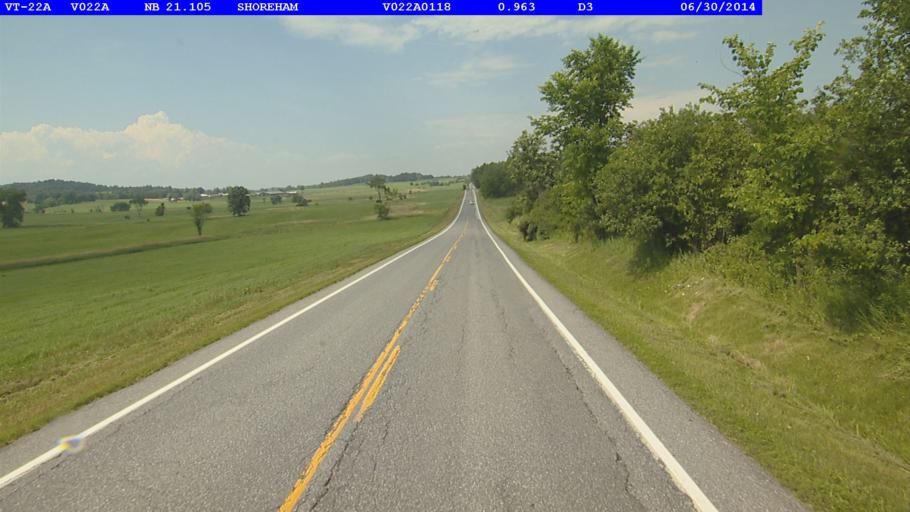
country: US
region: New York
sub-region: Essex County
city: Ticonderoga
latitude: 43.8633
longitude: -73.3096
